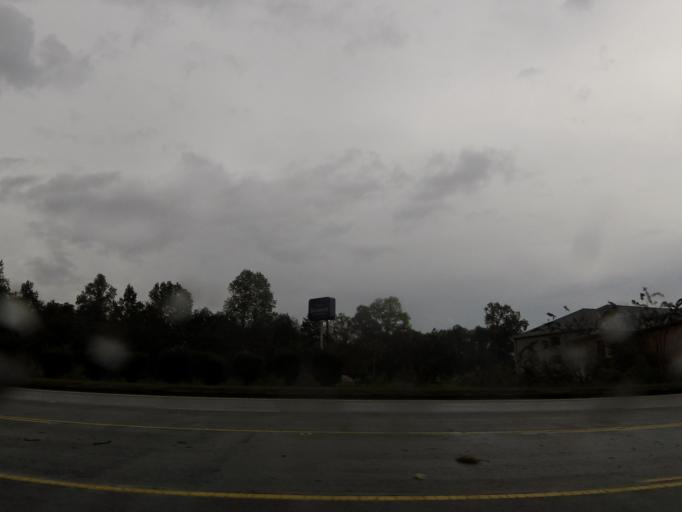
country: US
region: Georgia
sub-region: Wayne County
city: Jesup
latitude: 31.5979
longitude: -81.8702
